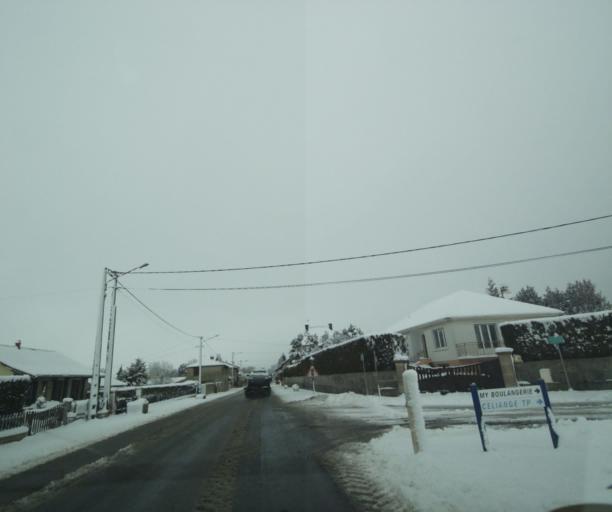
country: FR
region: Champagne-Ardenne
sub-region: Departement de la Haute-Marne
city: Saint-Dizier
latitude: 48.5811
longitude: 4.9047
